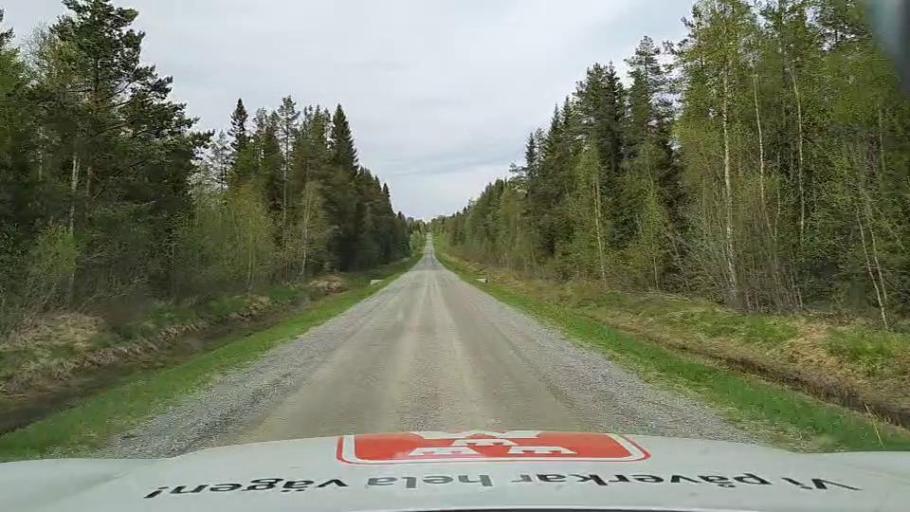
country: SE
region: Jaemtland
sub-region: OEstersunds Kommun
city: Brunflo
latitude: 62.6066
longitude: 14.9396
